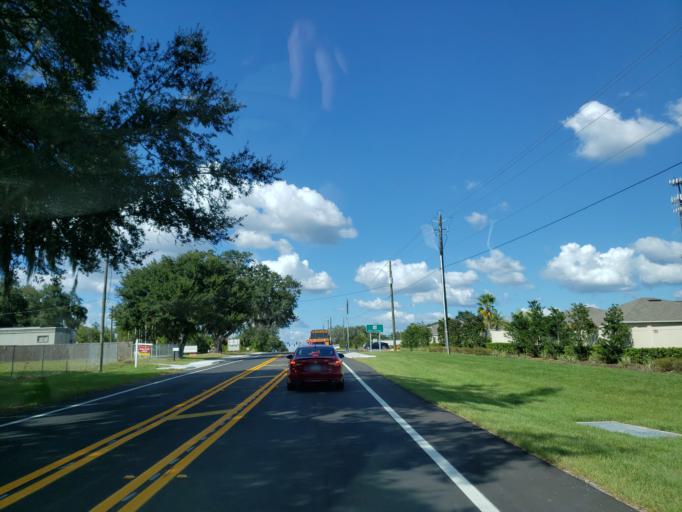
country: US
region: Florida
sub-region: Hillsborough County
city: Valrico
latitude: 27.9345
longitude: -82.2195
